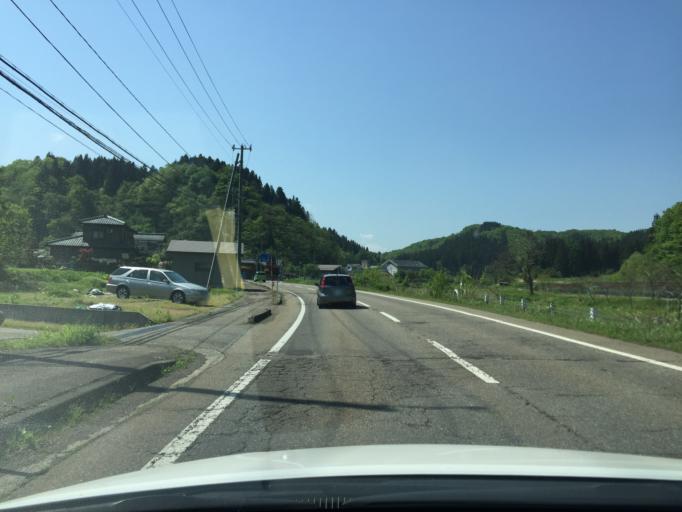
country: JP
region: Niigata
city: Kamo
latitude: 37.6196
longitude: 139.1042
